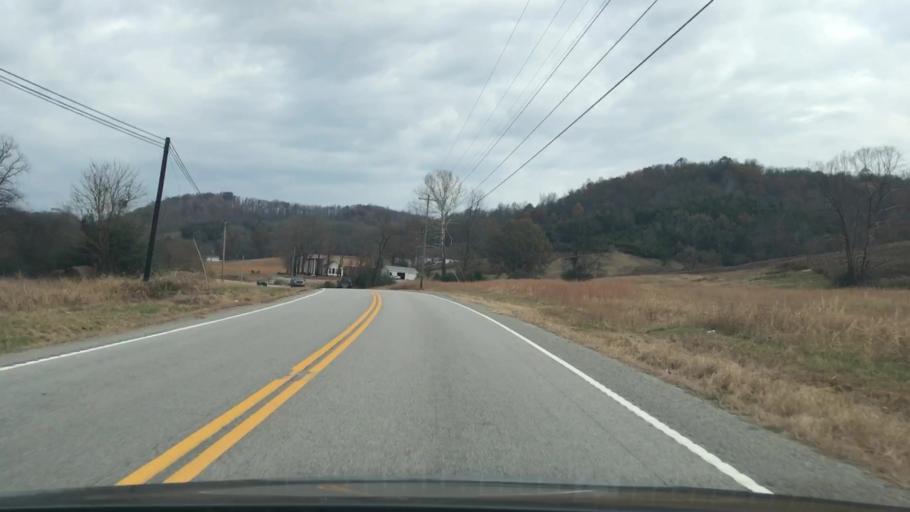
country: US
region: Tennessee
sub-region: Macon County
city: Lafayette
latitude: 36.4747
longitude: -86.0423
